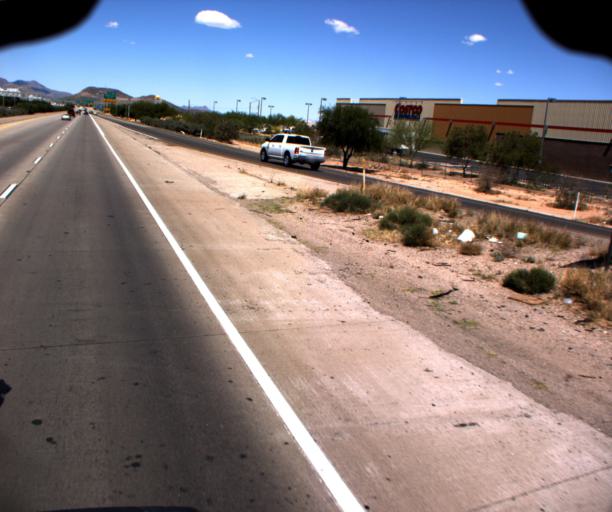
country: US
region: Arizona
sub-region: Pima County
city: South Tucson
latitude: 32.1787
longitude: -110.9468
